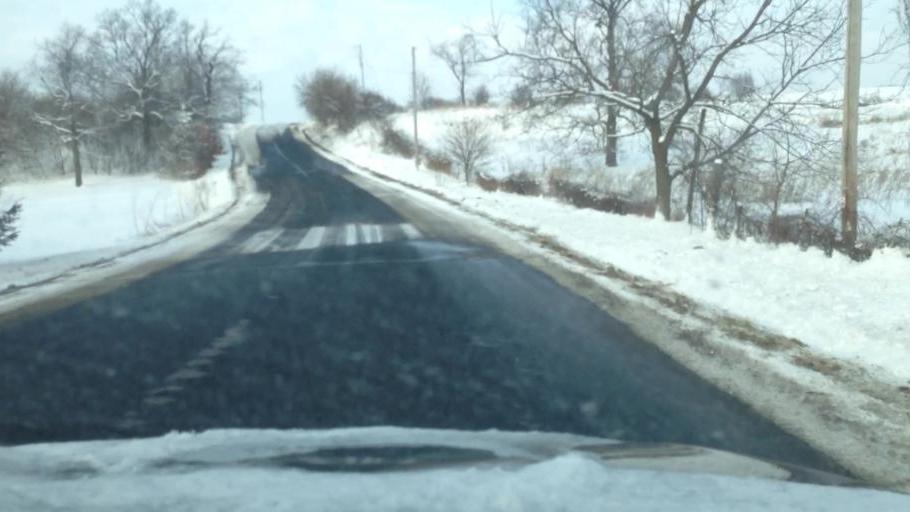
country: US
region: Wisconsin
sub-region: Walworth County
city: East Troy
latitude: 42.7550
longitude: -88.4455
